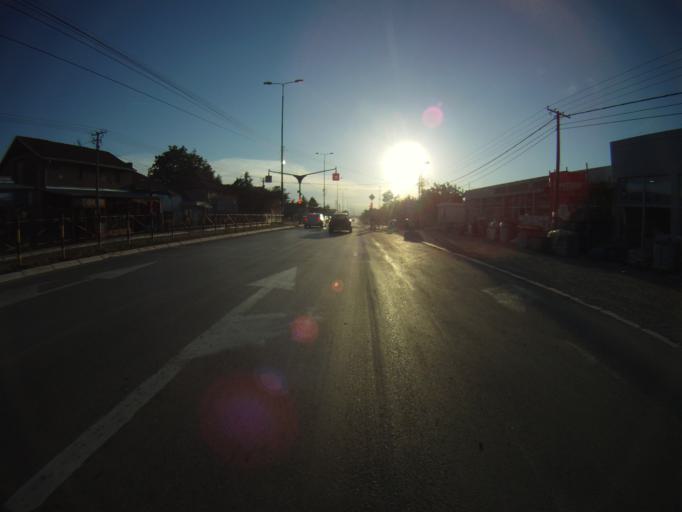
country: RS
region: Central Serbia
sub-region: Nisavski Okrug
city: Niska Banja
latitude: 43.3029
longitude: 21.9809
